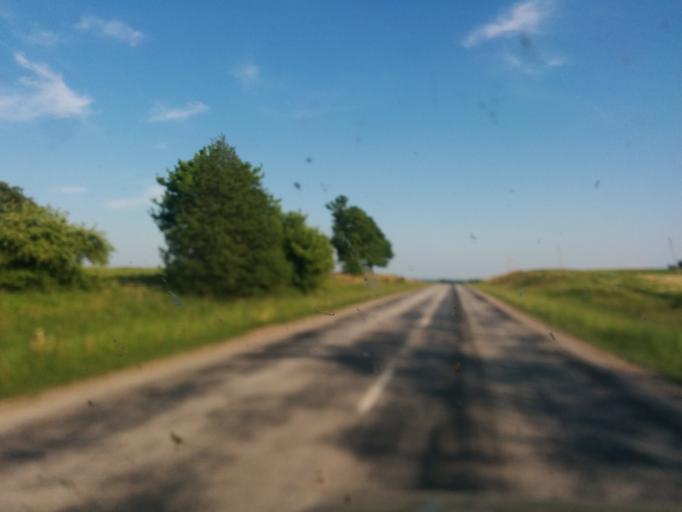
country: LV
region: Talsu Rajons
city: Valdemarpils
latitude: 57.3263
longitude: 22.5223
